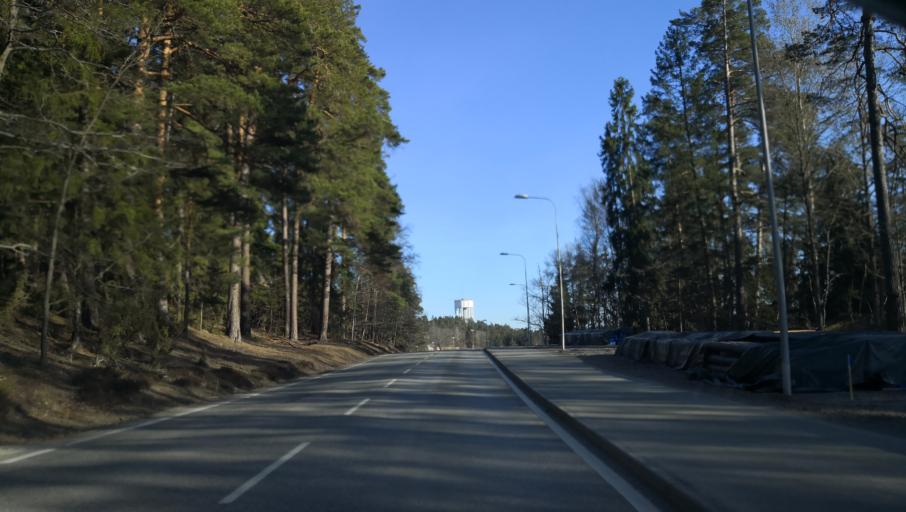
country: SE
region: Stockholm
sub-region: Varmdo Kommun
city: Gustavsberg
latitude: 59.3359
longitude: 18.3811
